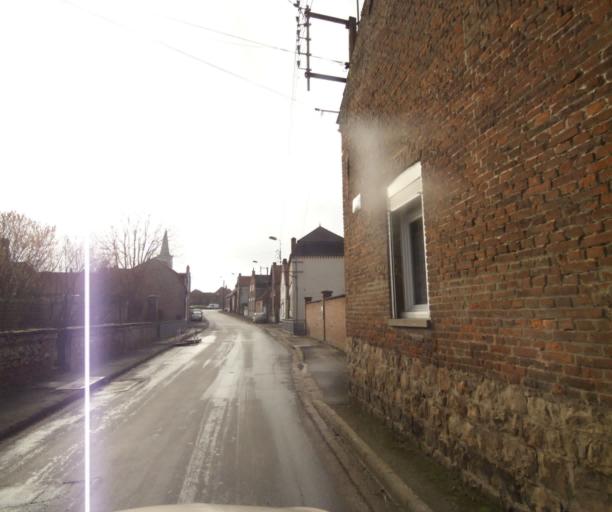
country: FR
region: Nord-Pas-de-Calais
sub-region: Departement du Nord
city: Vendegies-sur-Ecaillon
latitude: 50.2686
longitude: 3.4766
